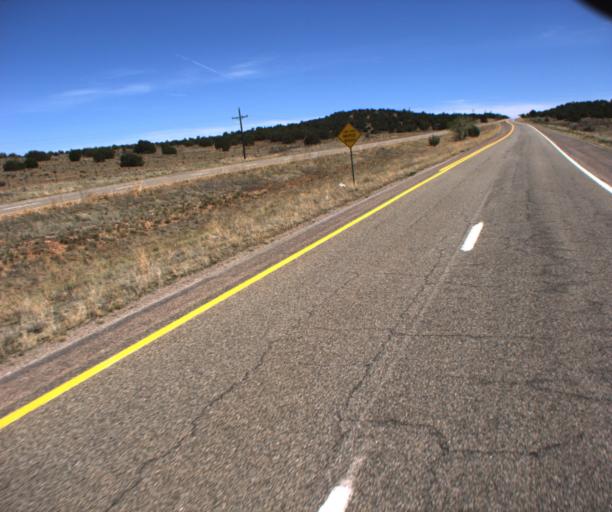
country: US
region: Arizona
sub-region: Mohave County
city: Peach Springs
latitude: 35.5293
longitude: -113.2287
